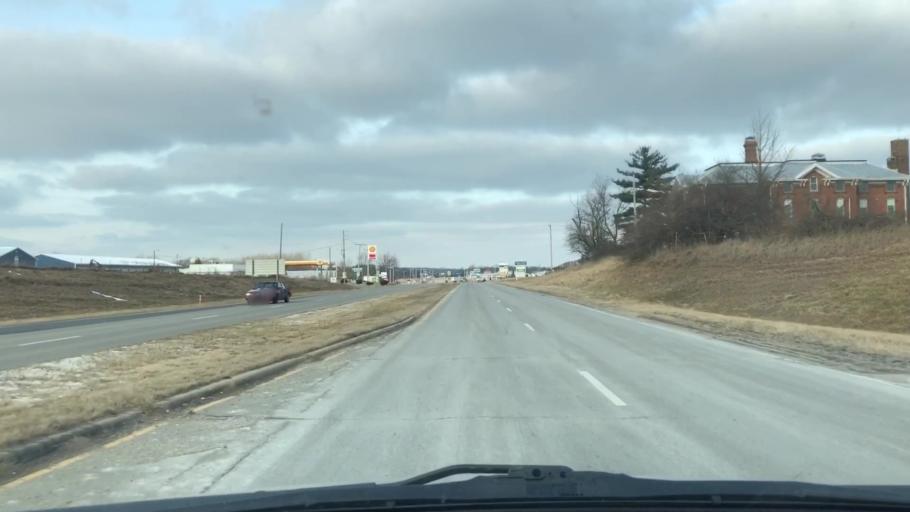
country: US
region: Indiana
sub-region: Steuben County
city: Angola
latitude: 41.6654
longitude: -85.0284
